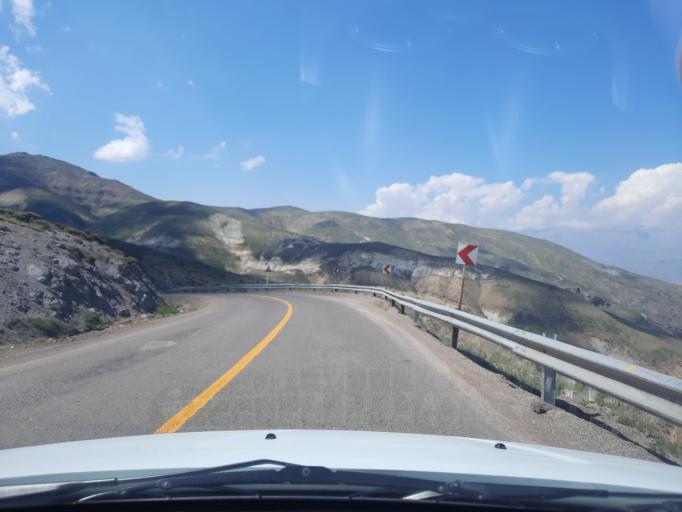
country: IR
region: Qazvin
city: Qazvin
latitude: 36.3971
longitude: 50.2151
